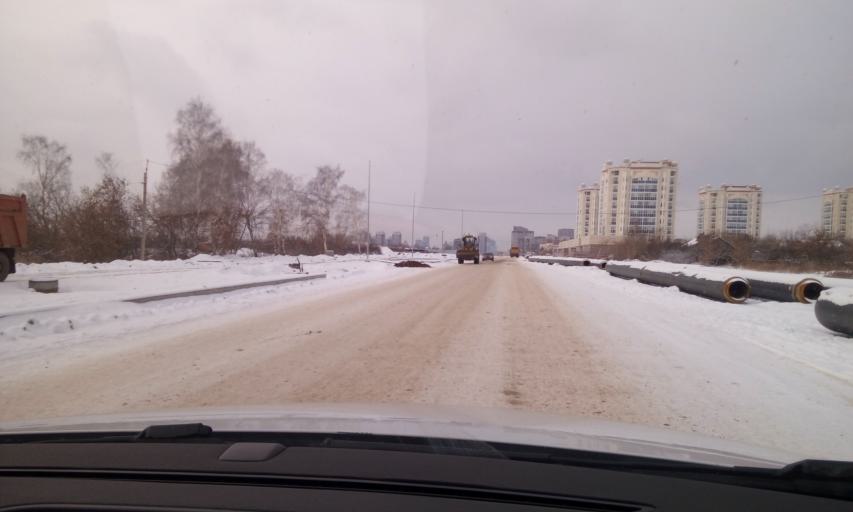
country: KZ
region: Astana Qalasy
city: Astana
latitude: 51.1184
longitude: 71.5089
